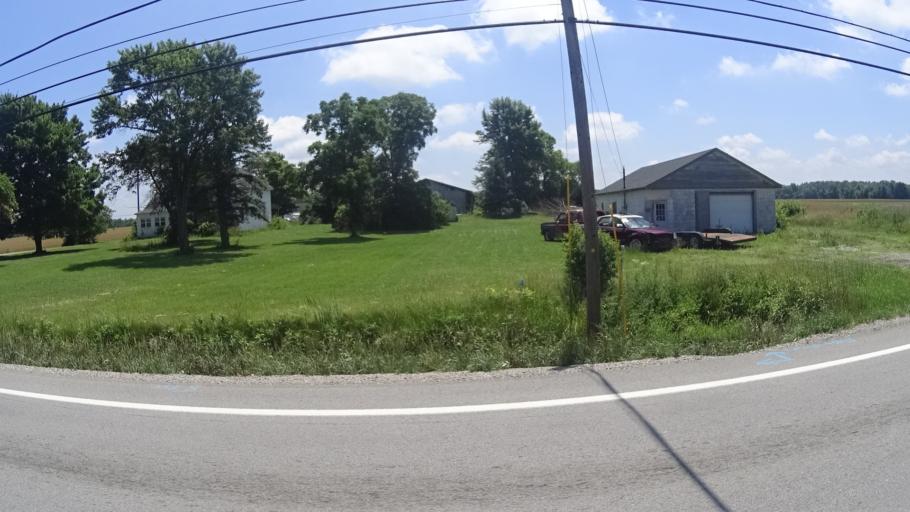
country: US
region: Ohio
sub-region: Huron County
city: Wakeman
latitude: 41.3288
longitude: -82.3730
